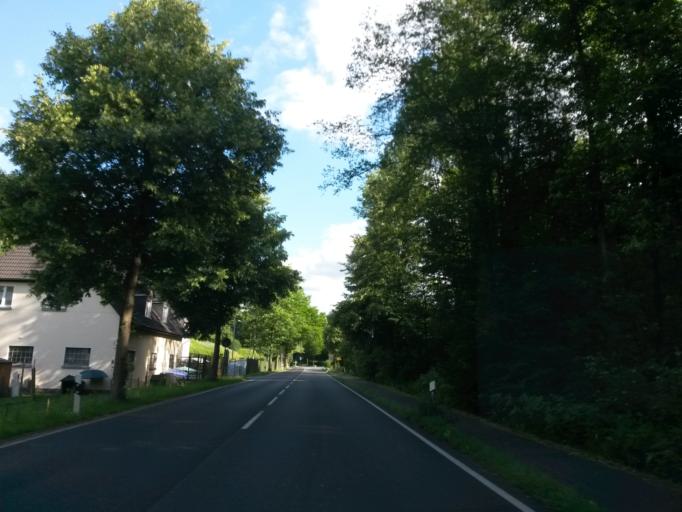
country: DE
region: North Rhine-Westphalia
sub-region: Regierungsbezirk Koln
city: Ruppichteroth
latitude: 50.8416
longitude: 7.4313
